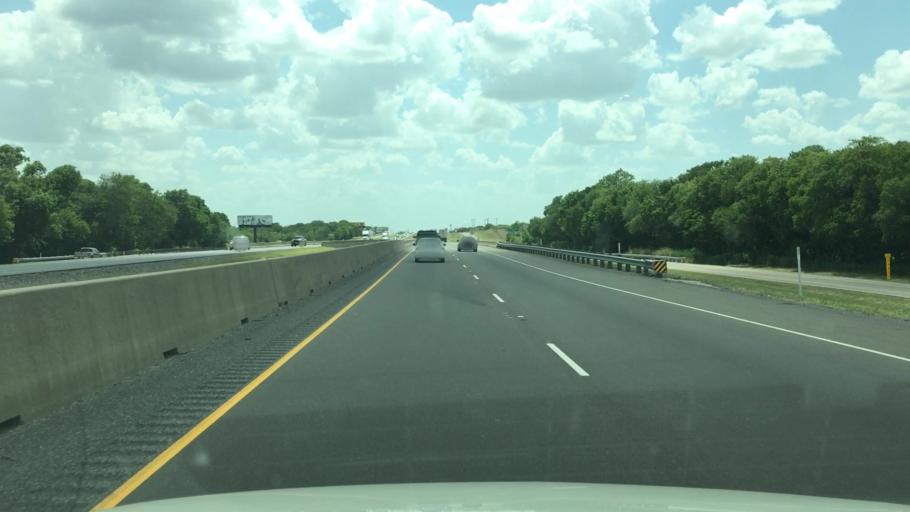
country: US
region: Texas
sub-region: Hunt County
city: Caddo Mills
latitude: 33.0156
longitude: -96.2111
